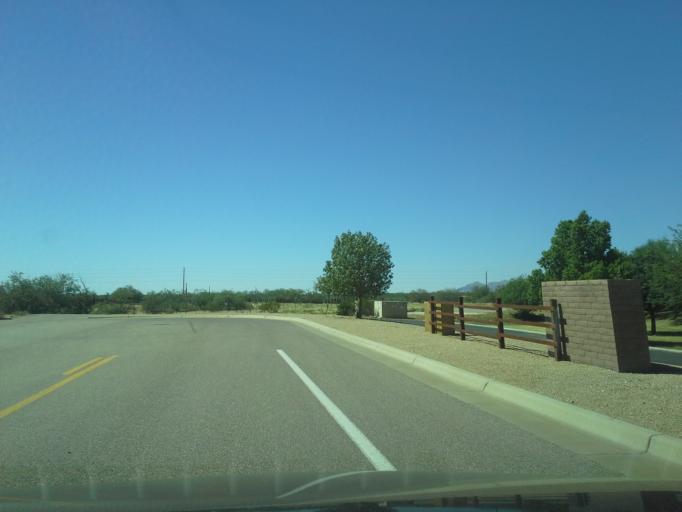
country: US
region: Arizona
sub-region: Pima County
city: Marana
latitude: 32.4666
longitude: -111.2152
